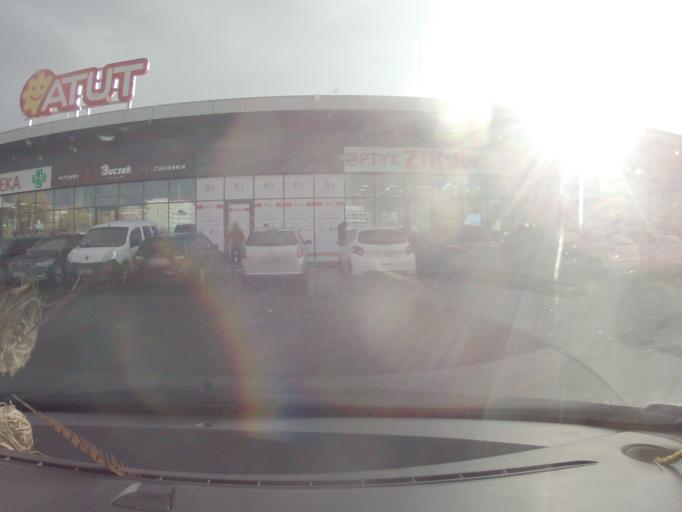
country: PL
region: Lesser Poland Voivodeship
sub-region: Krakow
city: Sidzina
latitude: 50.0119
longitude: 19.8863
